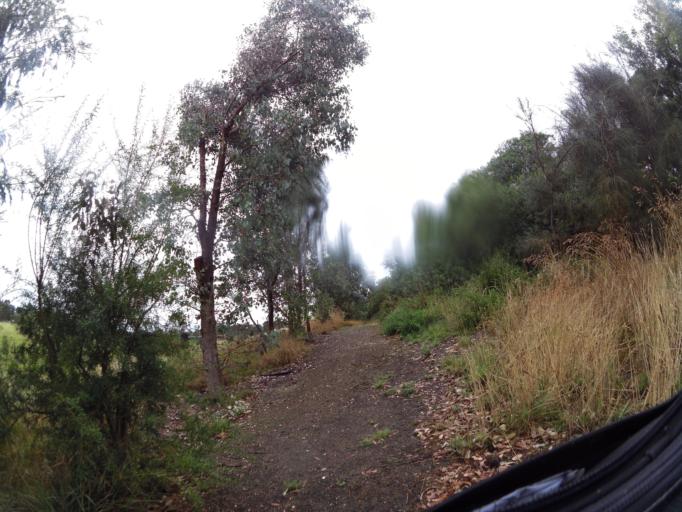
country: AU
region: Victoria
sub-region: East Gippsland
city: Bairnsdale
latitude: -37.8119
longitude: 147.7435
